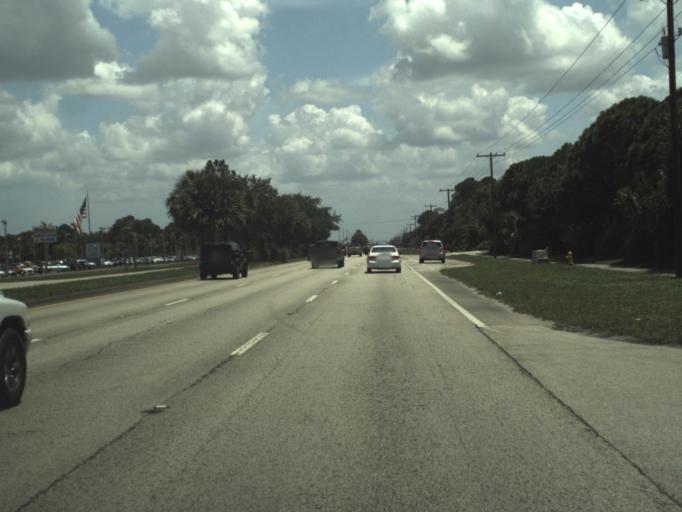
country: US
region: Florida
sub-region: Martin County
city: Port Salerno
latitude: 27.1610
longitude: -80.2242
